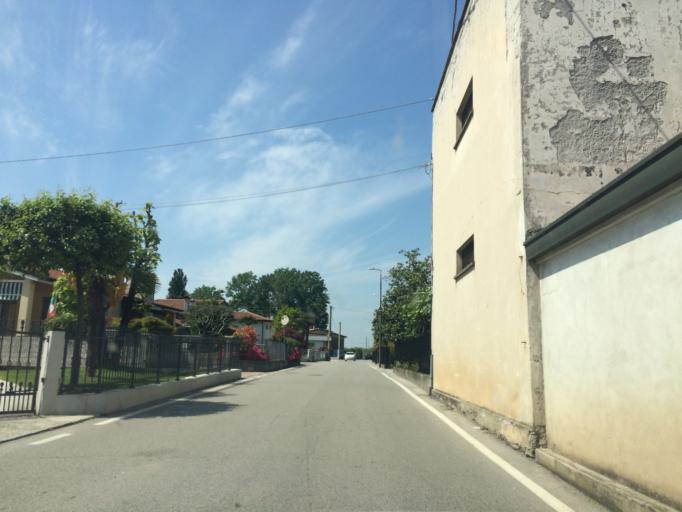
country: IT
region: Veneto
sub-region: Provincia di Padova
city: Fontaniva
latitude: 45.6336
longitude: 11.7556
